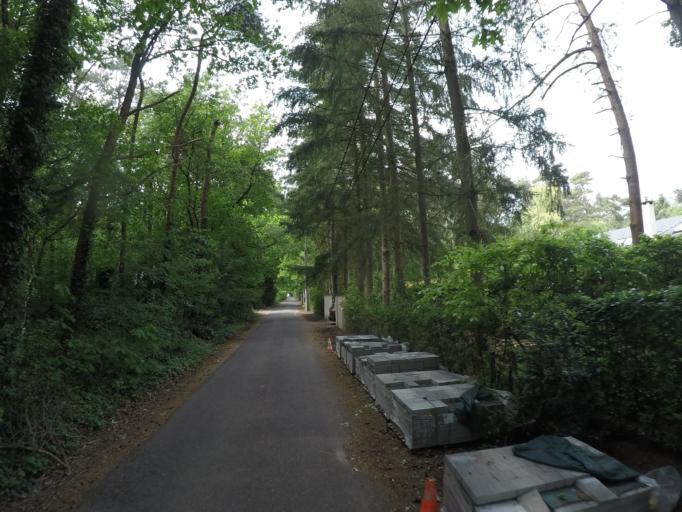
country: BE
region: Flanders
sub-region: Provincie Antwerpen
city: Zoersel
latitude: 51.2742
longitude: 4.7040
